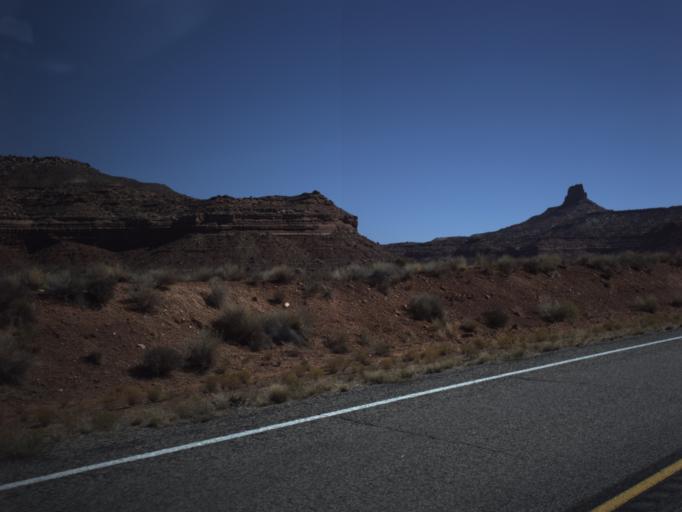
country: US
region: Utah
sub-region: San Juan County
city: Blanding
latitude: 37.7334
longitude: -110.2597
